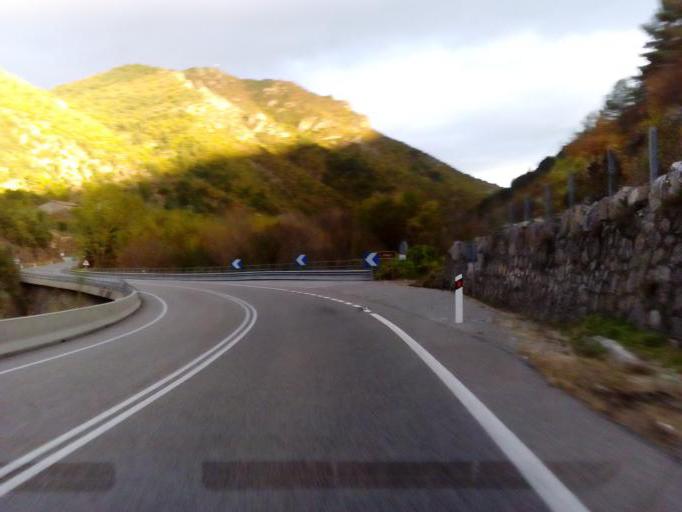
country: ES
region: Catalonia
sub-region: Provincia de Lleida
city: Toloriu
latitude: 42.3743
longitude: 1.6341
